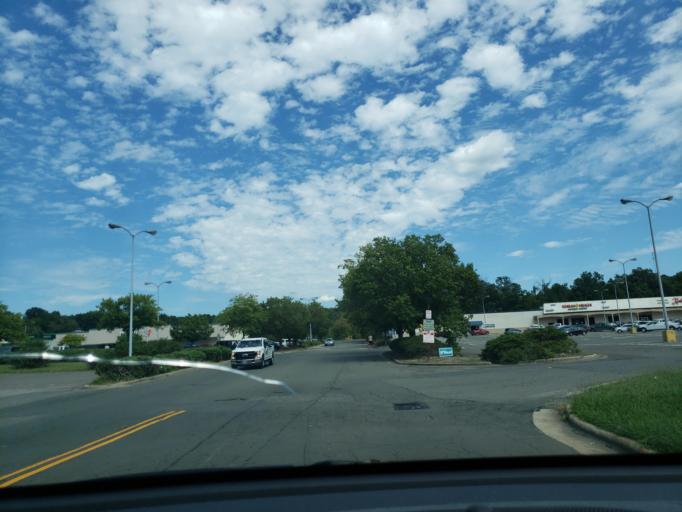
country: US
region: North Carolina
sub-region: Durham County
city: Durham
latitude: 36.0165
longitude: -78.8874
